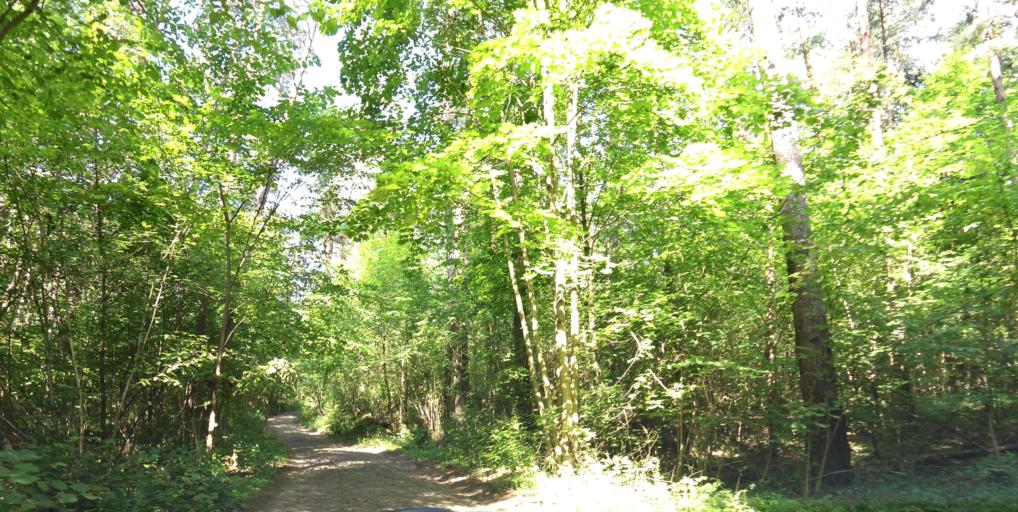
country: LT
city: Grigiskes
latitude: 54.7402
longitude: 25.0326
